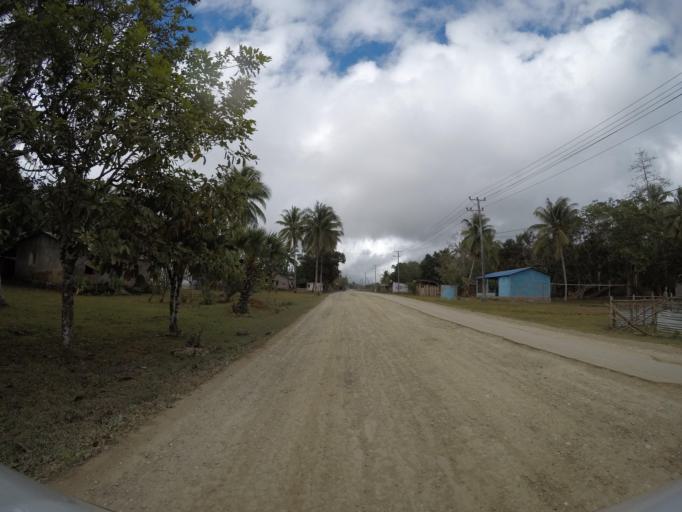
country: TL
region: Lautem
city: Lospalos
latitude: -8.5032
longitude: 126.9895
